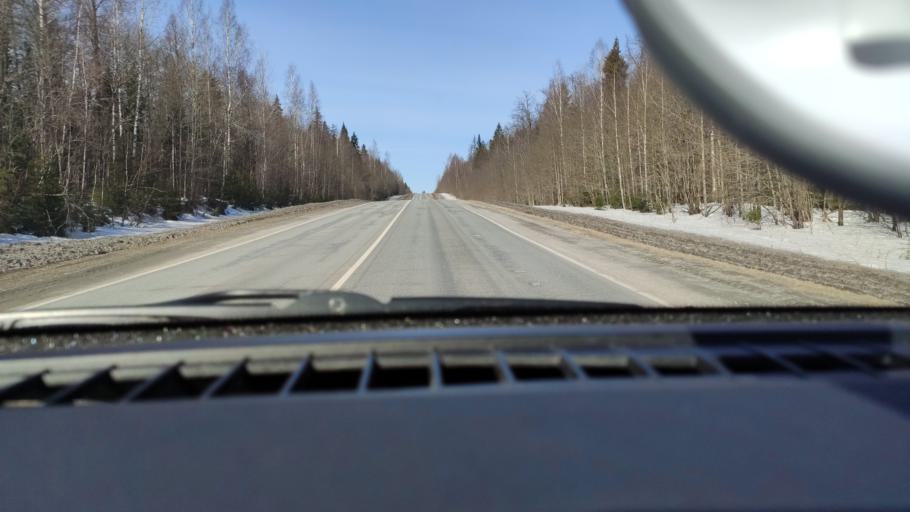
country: RU
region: Perm
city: Perm
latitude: 58.1754
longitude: 56.2302
